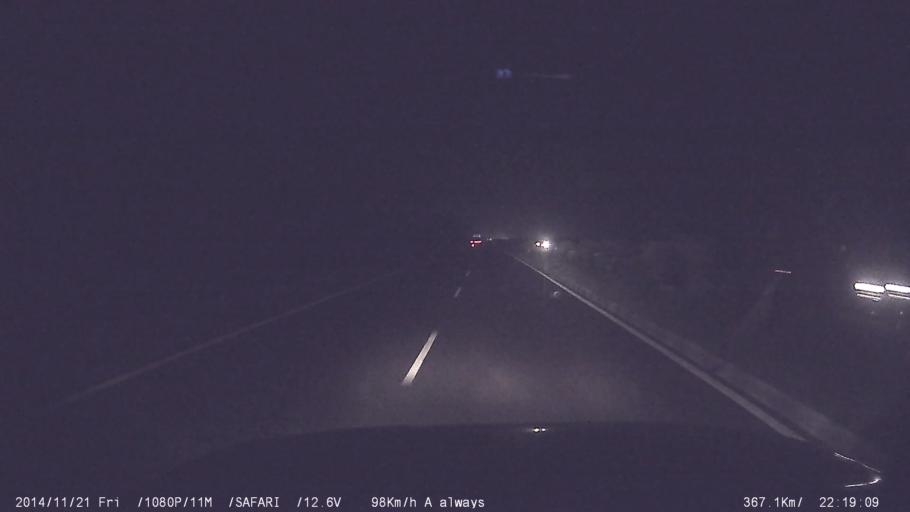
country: IN
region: Tamil Nadu
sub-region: Kancheepuram
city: Madurantakam
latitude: 12.3873
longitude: 79.7976
